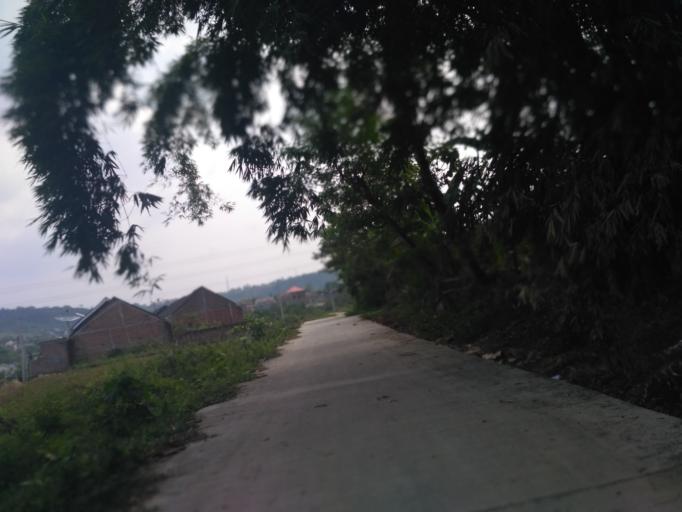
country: ID
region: Central Java
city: Mranggen
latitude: -7.0677
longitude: 110.4631
